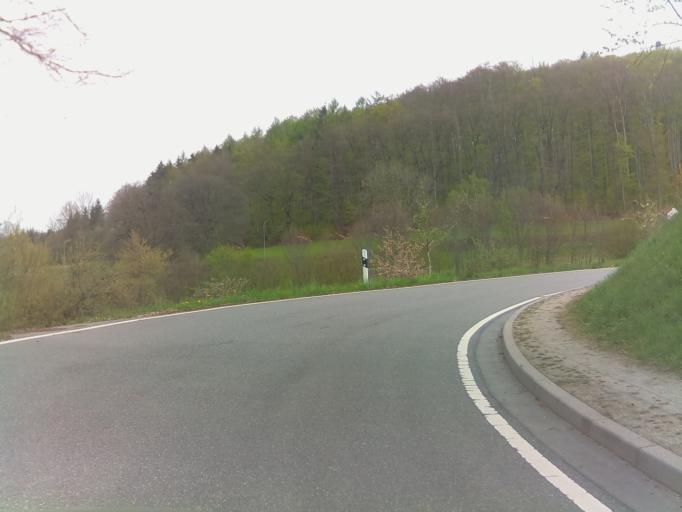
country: DE
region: Hesse
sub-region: Regierungsbezirk Darmstadt
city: Lindenfels
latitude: 49.6912
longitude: 8.7226
